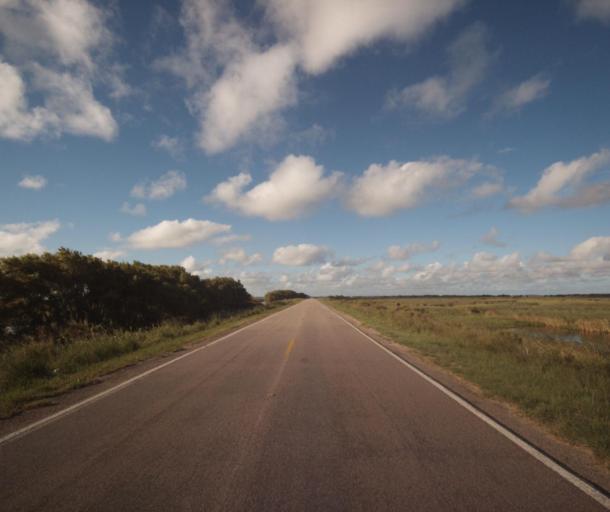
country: BR
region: Rio Grande do Sul
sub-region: Arroio Grande
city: Arroio Grande
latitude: -32.6035
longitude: -52.5704
